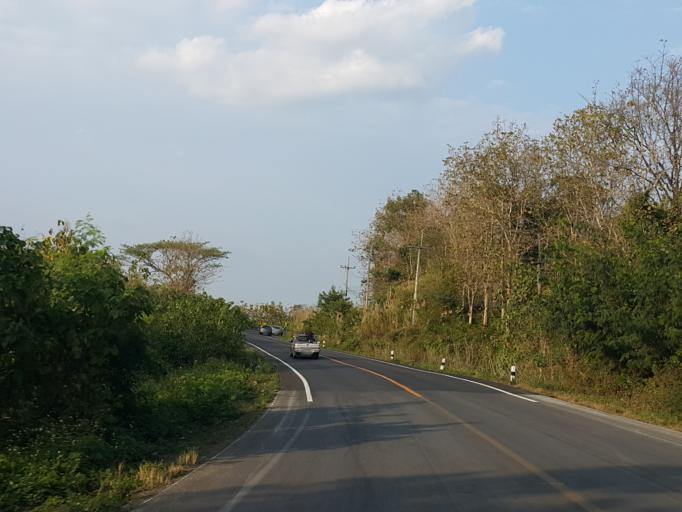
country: TH
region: Lampang
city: Lampang
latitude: 18.4698
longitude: 99.4633
